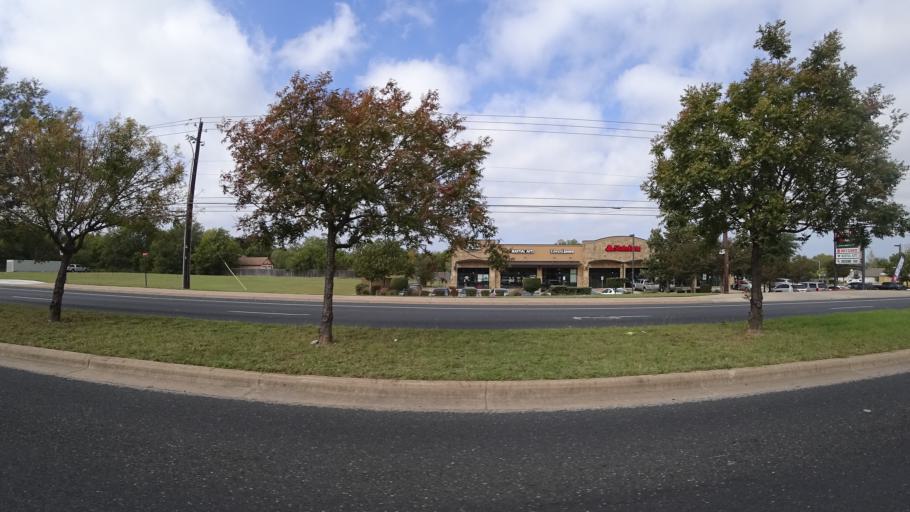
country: US
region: Texas
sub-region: Travis County
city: Shady Hollow
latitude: 30.1998
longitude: -97.8393
